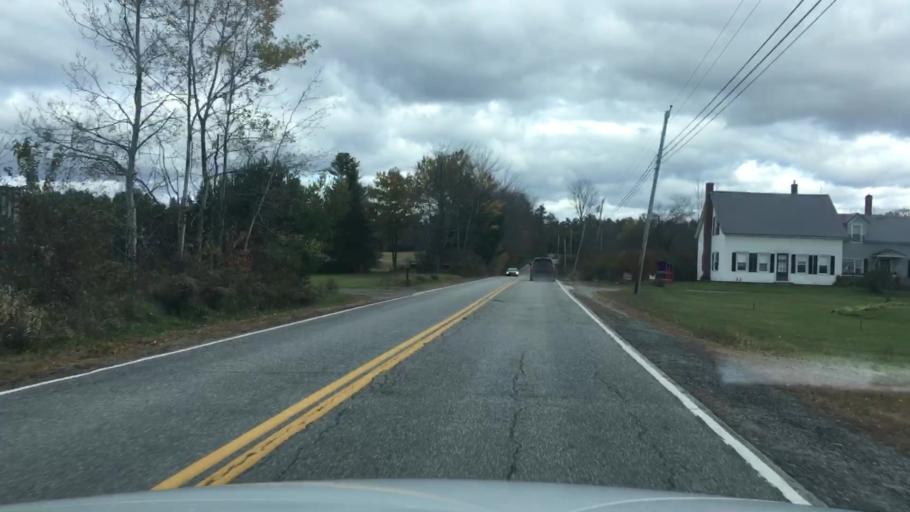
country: US
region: Maine
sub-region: Sagadahoc County
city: Richmond
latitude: 44.1229
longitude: -69.9054
